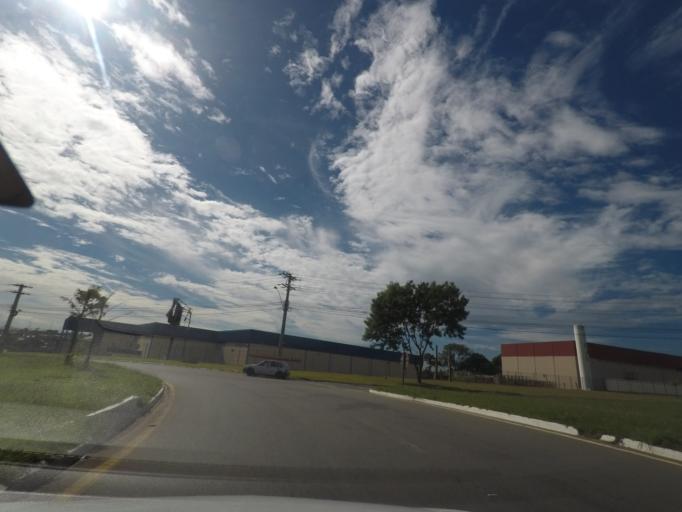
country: BR
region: Goias
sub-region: Aparecida De Goiania
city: Aparecida de Goiania
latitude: -16.7888
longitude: -49.2515
